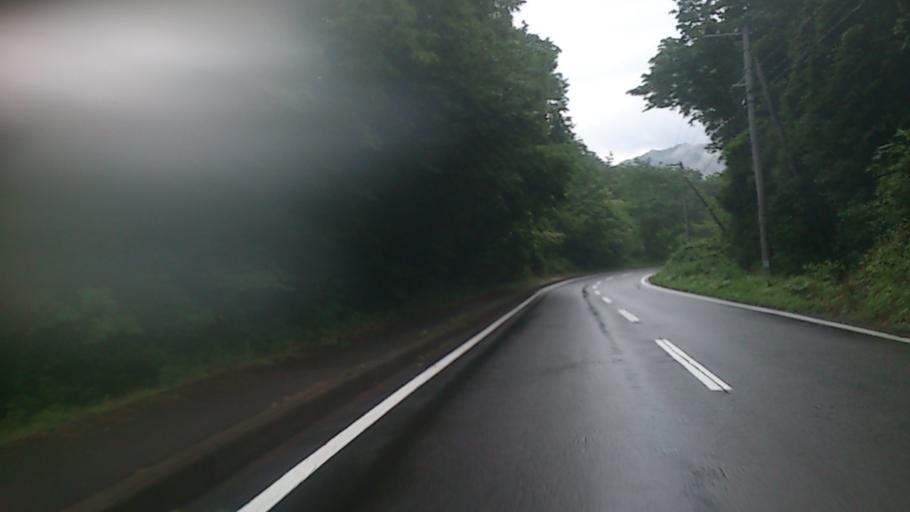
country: JP
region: Akita
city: Noshiromachi
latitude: 40.5548
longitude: 139.9539
